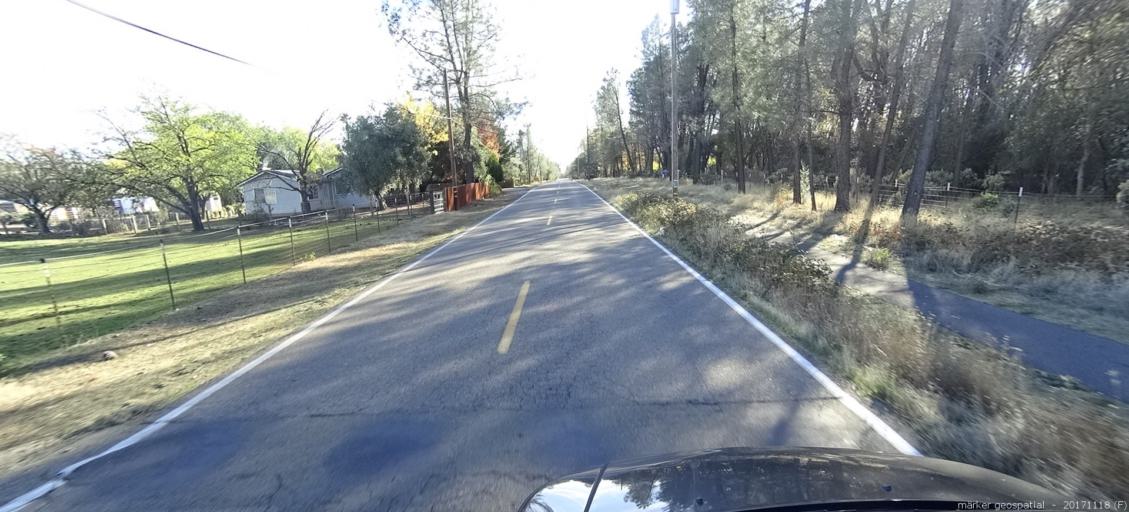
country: US
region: California
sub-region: Shasta County
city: Redding
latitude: 40.4578
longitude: -122.4546
